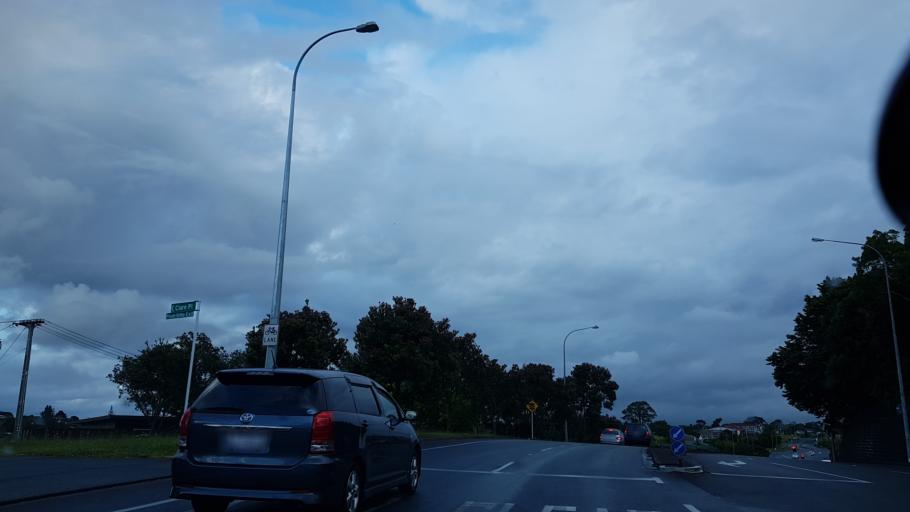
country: NZ
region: Auckland
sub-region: Auckland
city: North Shore
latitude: -36.7759
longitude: 174.7221
